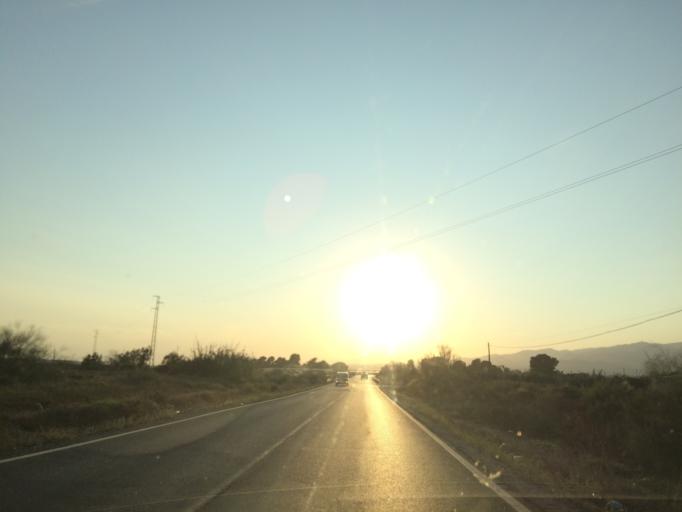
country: ES
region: Andalusia
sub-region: Provincia de Almeria
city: Nijar
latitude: 36.9324
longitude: -2.1136
